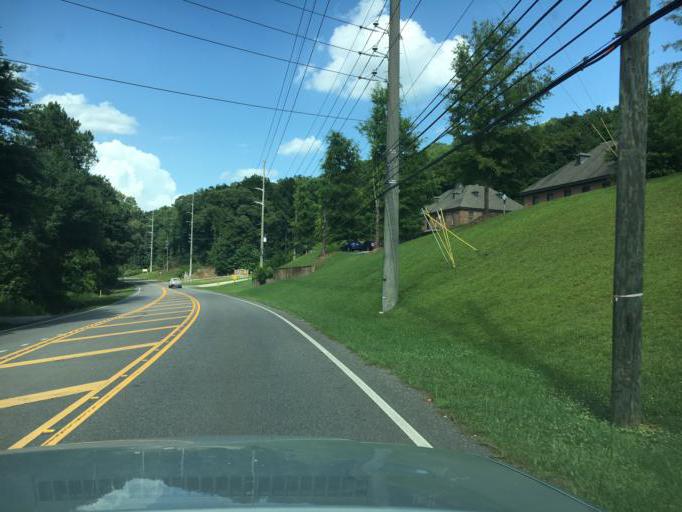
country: US
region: Alabama
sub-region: Shelby County
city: Indian Springs Village
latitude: 33.3840
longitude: -86.7322
